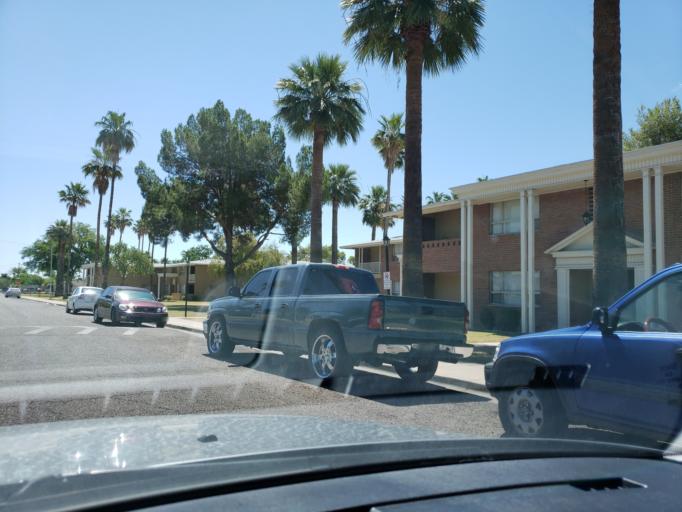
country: US
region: Arizona
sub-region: Maricopa County
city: Phoenix
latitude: 33.5059
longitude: -112.0929
